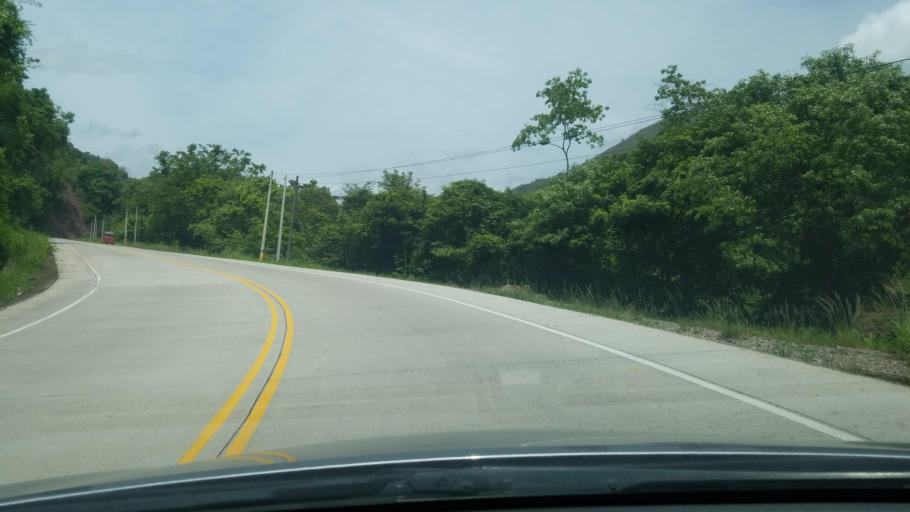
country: HN
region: Copan
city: Veracruz
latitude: 14.8822
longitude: -88.7756
